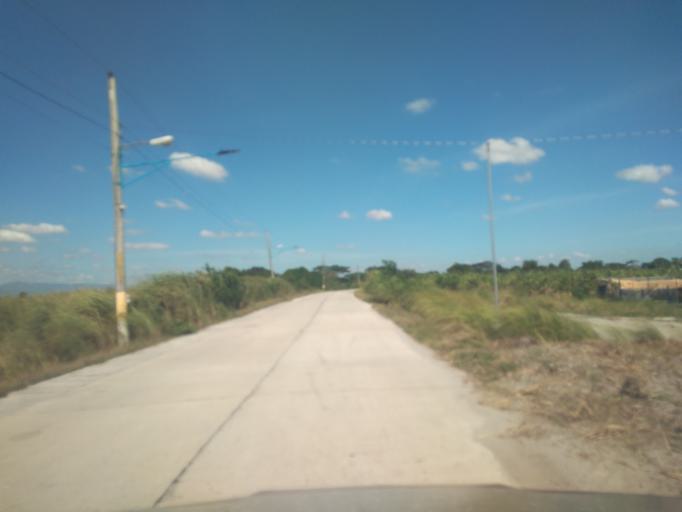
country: PH
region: Central Luzon
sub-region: Province of Pampanga
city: Balas
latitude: 15.0461
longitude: 120.6131
